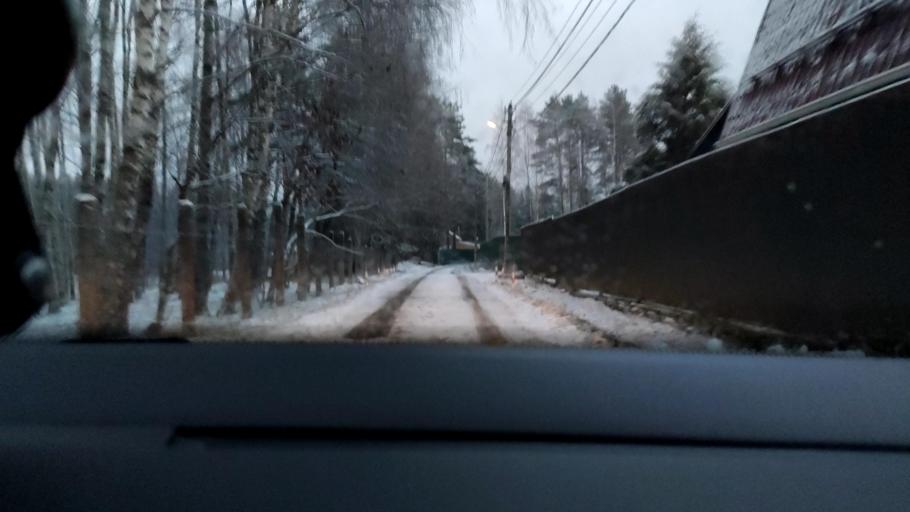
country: RU
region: Moskovskaya
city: Kubinka
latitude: 55.5165
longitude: 36.7021
